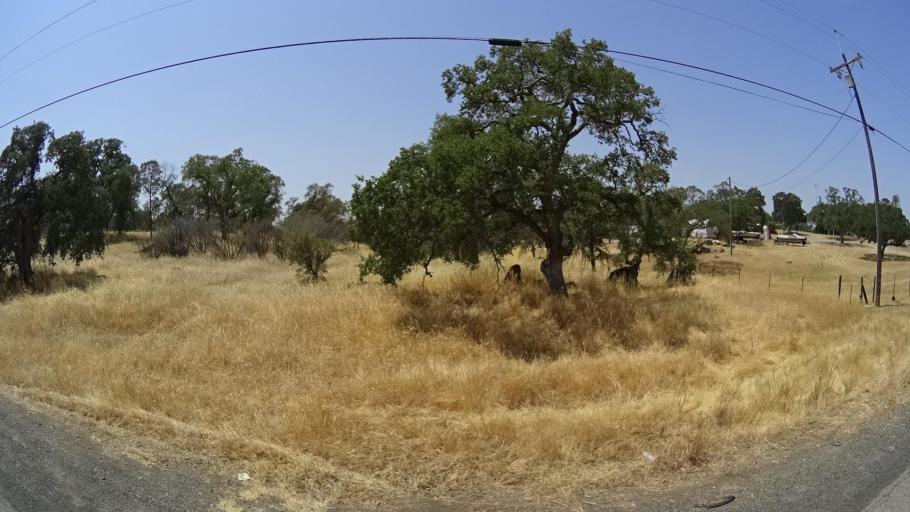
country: US
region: California
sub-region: Tuolumne County
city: Tuolumne City
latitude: 37.6623
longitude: -120.3138
